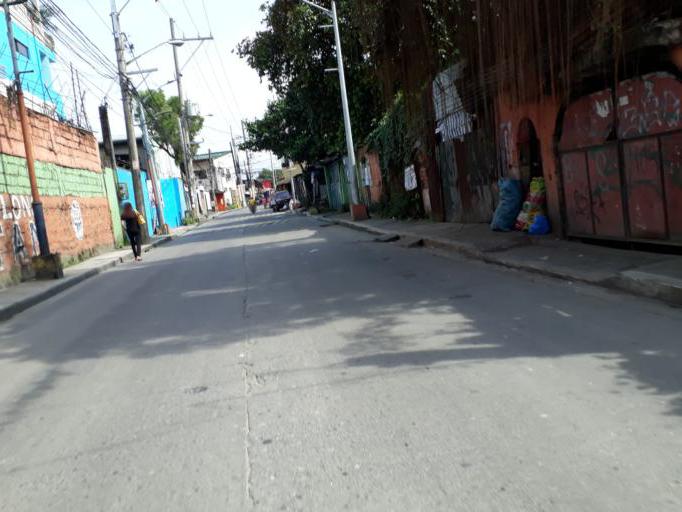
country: PH
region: Calabarzon
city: Bagong Pagasa
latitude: 14.6745
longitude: 121.0046
